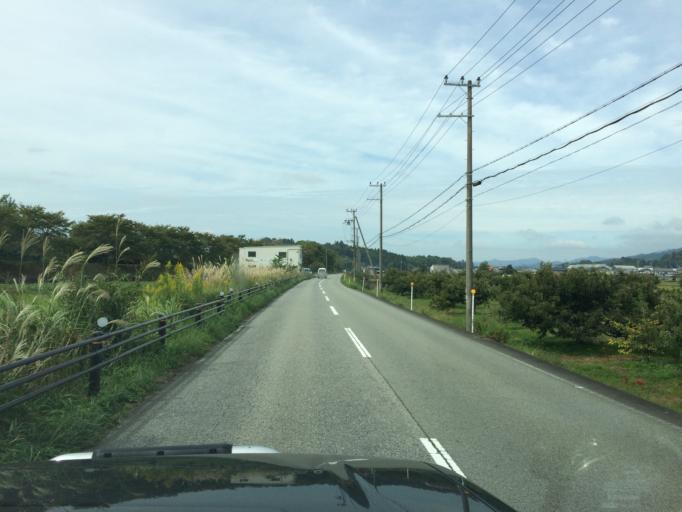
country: JP
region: Hyogo
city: Sasayama
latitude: 35.0734
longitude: 135.2402
